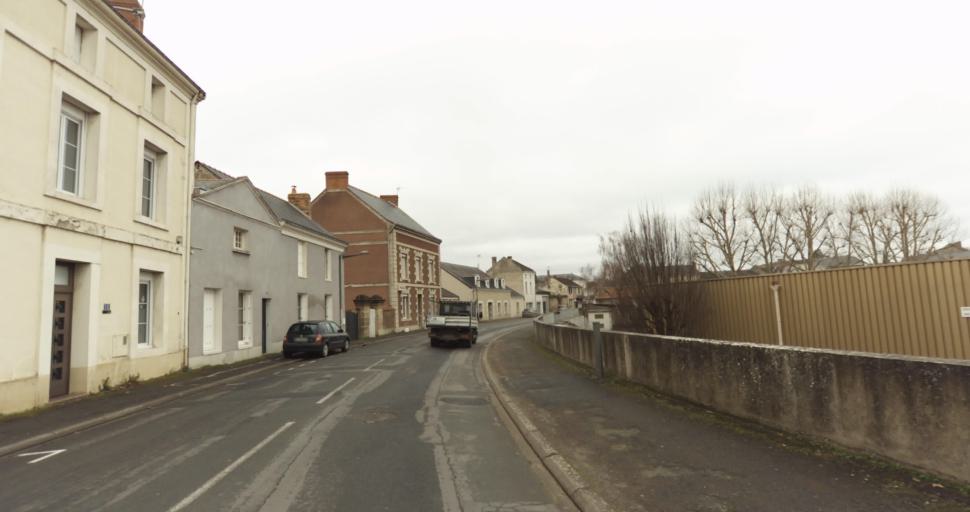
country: FR
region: Pays de la Loire
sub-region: Departement de Maine-et-Loire
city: Doue-la-Fontaine
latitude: 47.1906
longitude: -0.2742
